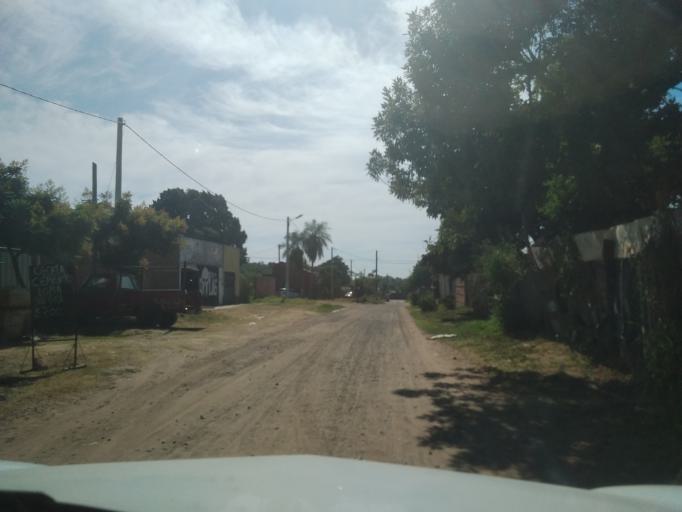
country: AR
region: Corrientes
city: Corrientes
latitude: -27.5110
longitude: -58.8064
